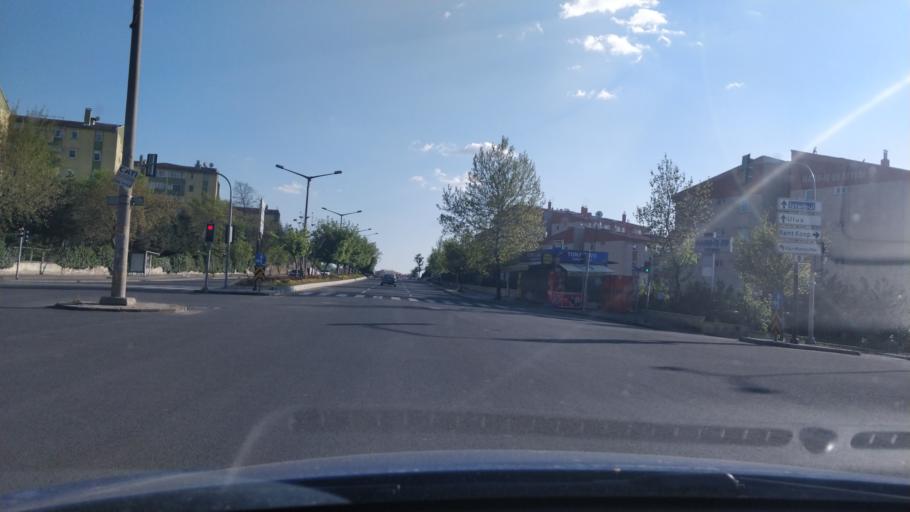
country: TR
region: Ankara
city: Batikent
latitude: 39.9619
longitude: 32.7321
